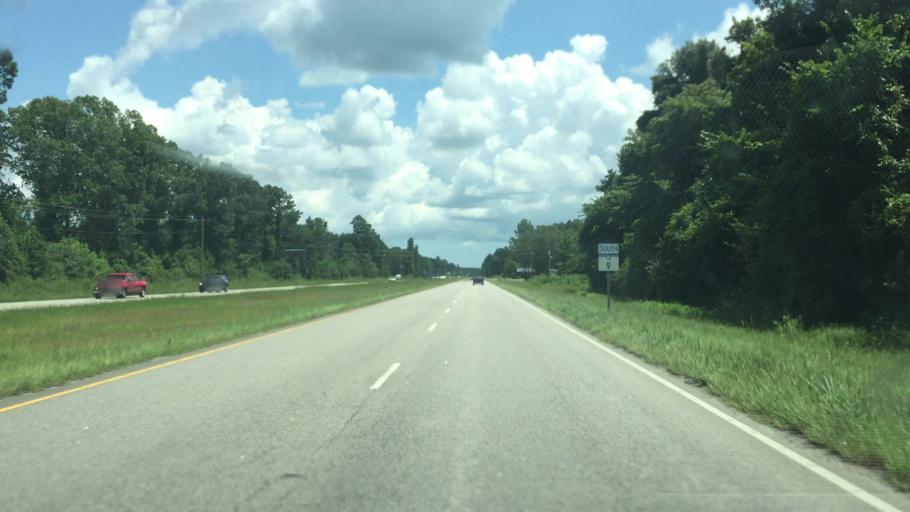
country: US
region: South Carolina
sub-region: Horry County
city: Loris
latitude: 34.0156
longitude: -78.7880
